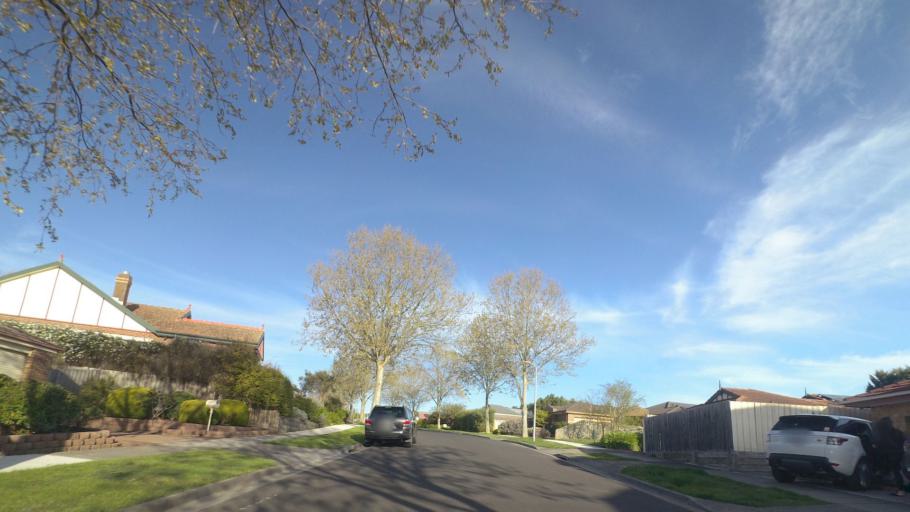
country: AU
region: Victoria
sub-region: Knox
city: Bayswater
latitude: -37.8560
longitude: 145.2576
